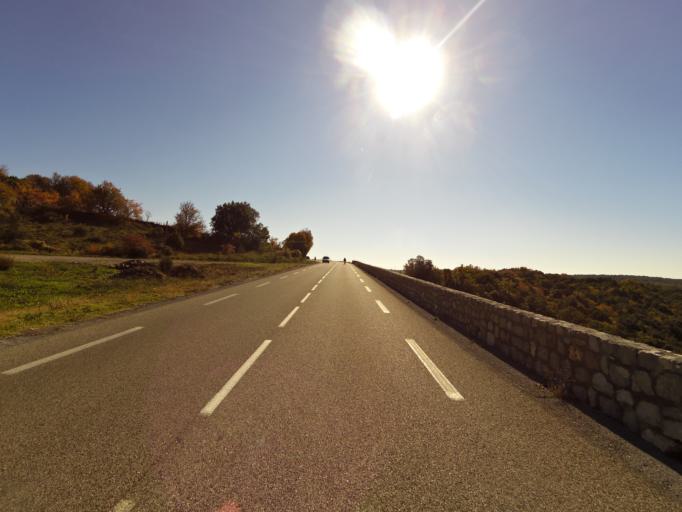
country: FR
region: Languedoc-Roussillon
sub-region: Departement du Gard
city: Saint-Julien-de-Peyrolas
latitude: 44.3993
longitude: 4.4804
